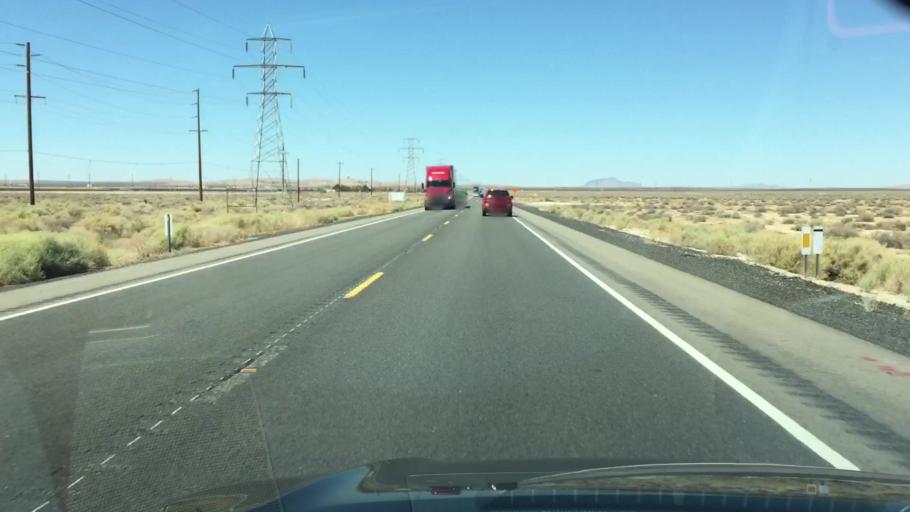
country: US
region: California
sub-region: Kern County
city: Boron
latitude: 35.0016
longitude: -117.5444
